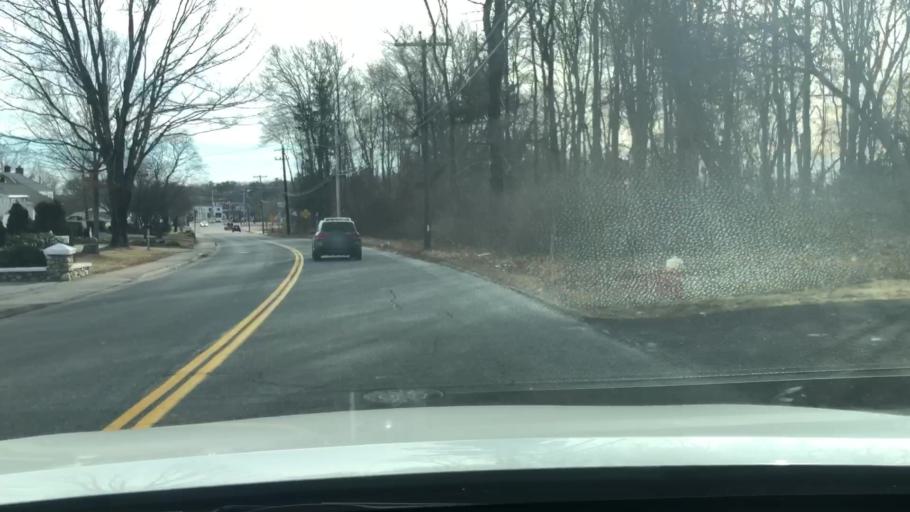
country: US
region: Massachusetts
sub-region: Worcester County
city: Hopedale
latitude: 42.1416
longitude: -71.5367
